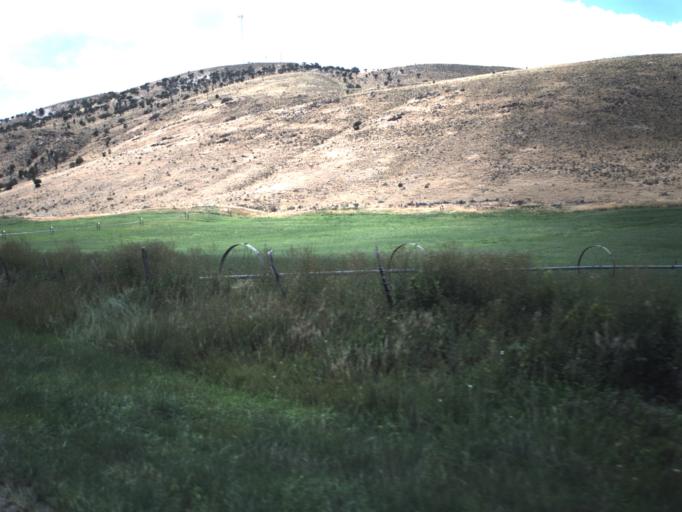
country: US
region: Utah
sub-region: Sanpete County
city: Gunnison
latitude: 39.1597
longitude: -111.7076
